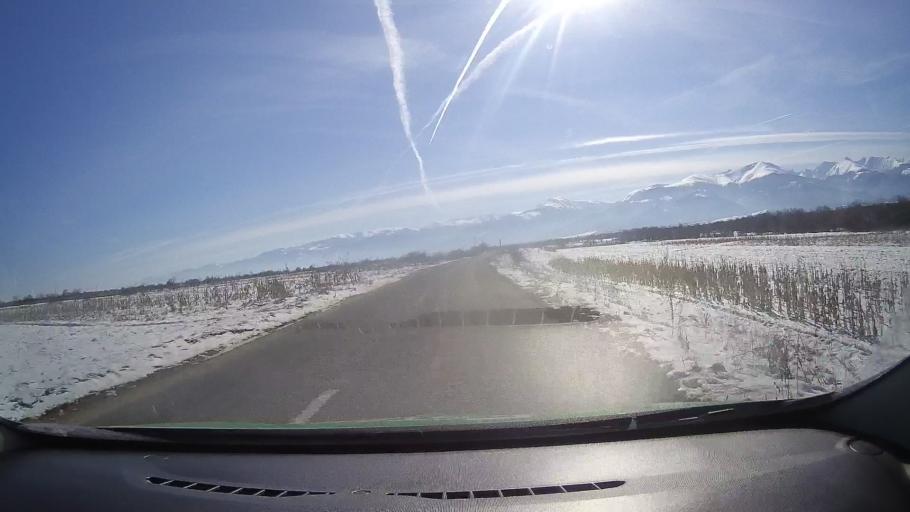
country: RO
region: Brasov
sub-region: Comuna Sambata de Sus
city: Sambata de Sus
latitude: 45.7537
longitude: 24.8345
